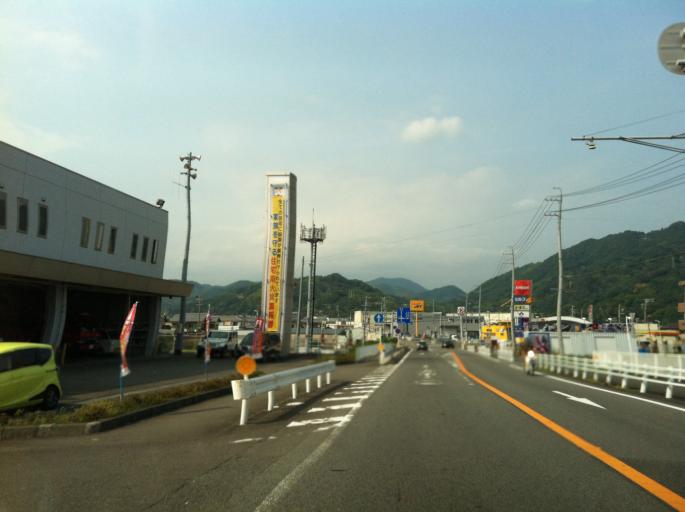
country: JP
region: Shizuoka
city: Fujieda
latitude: 34.8983
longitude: 138.2848
